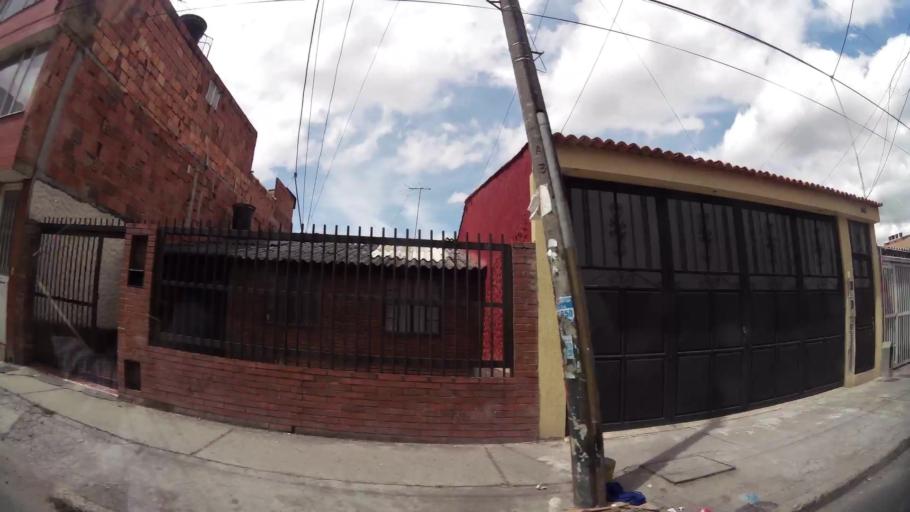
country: CO
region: Bogota D.C.
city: Barrio San Luis
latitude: 4.7025
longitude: -74.1109
